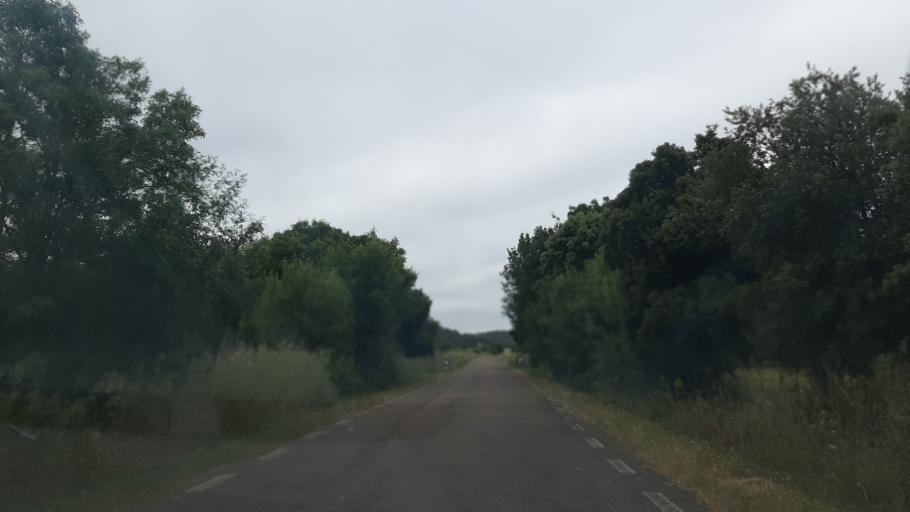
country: ES
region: Castille and Leon
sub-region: Provincia de Salamanca
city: Pastores
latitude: 40.5592
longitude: -6.4864
